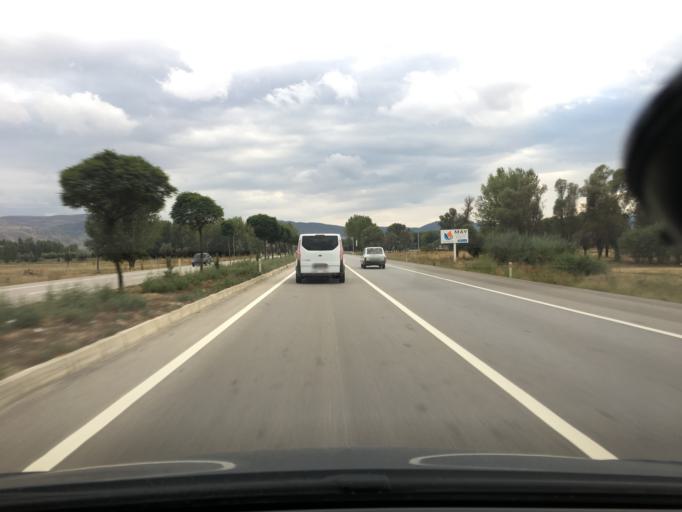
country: TR
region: Afyonkarahisar
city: Sincanli
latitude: 38.7524
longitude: 30.3589
